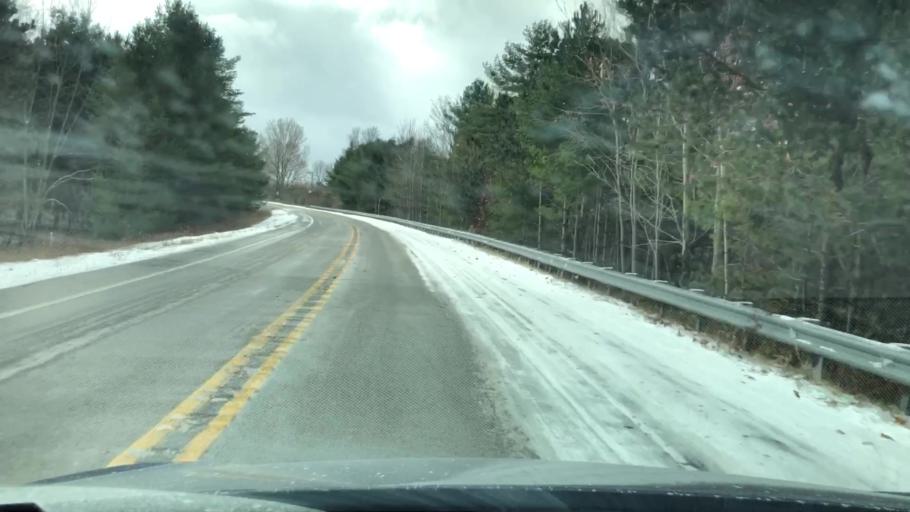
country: US
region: Michigan
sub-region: Antrim County
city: Elk Rapids
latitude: 44.9786
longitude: -85.5033
